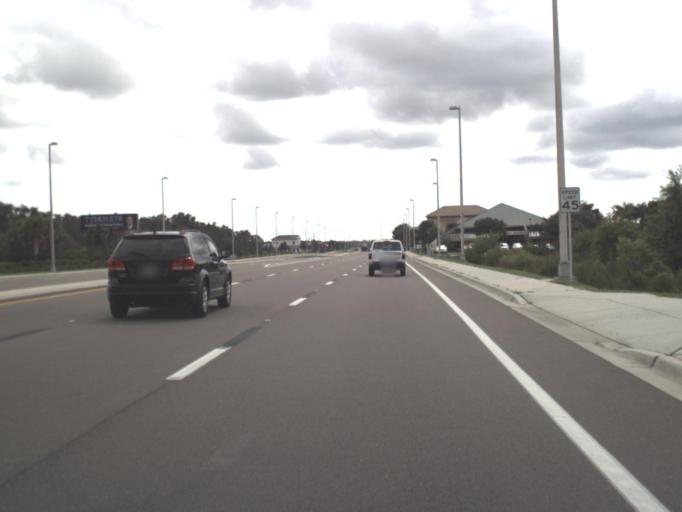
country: US
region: Florida
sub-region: Lee County
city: Villas
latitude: 26.5406
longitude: -81.8529
